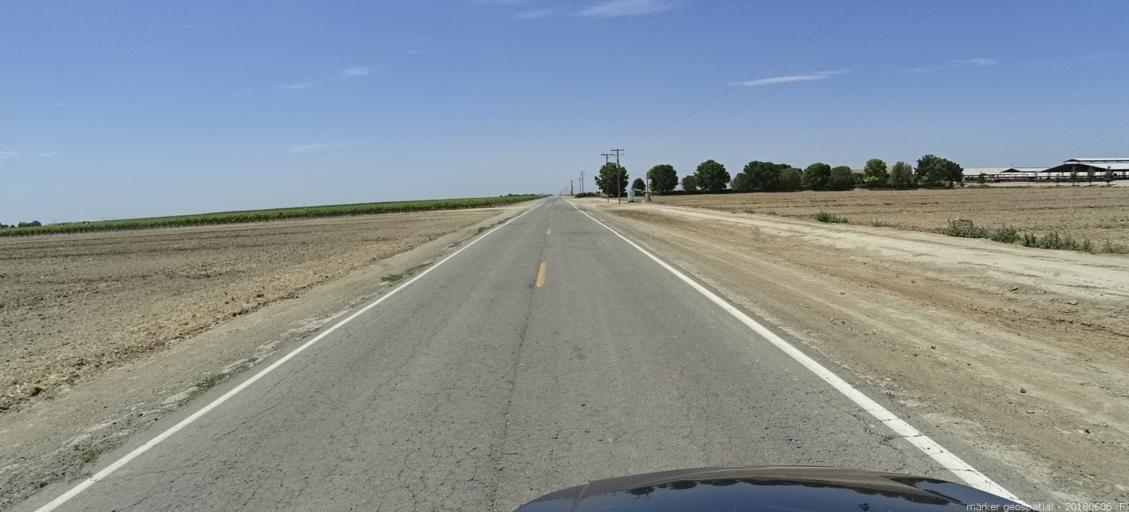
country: US
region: California
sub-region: Fresno County
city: Firebaugh
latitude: 36.9391
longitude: -120.3824
